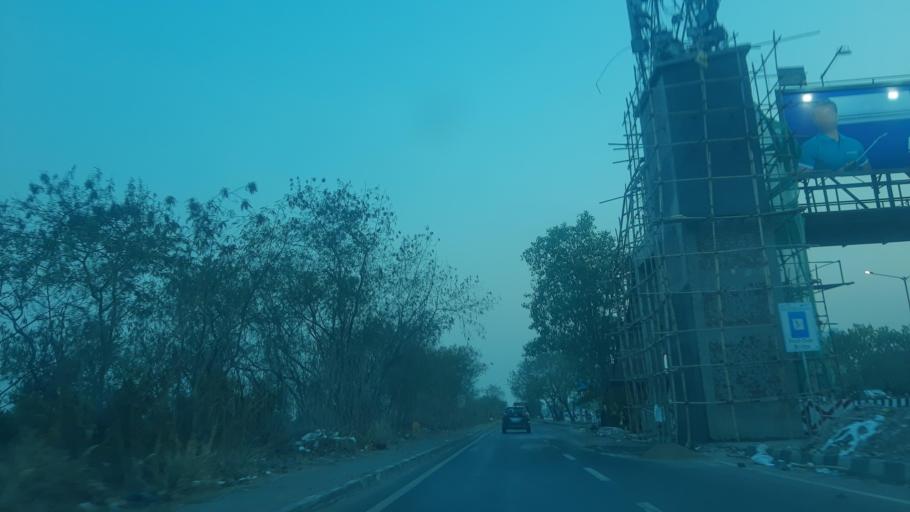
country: IN
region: Maharashtra
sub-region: Thane
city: Airoli
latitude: 19.1449
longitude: 72.9511
